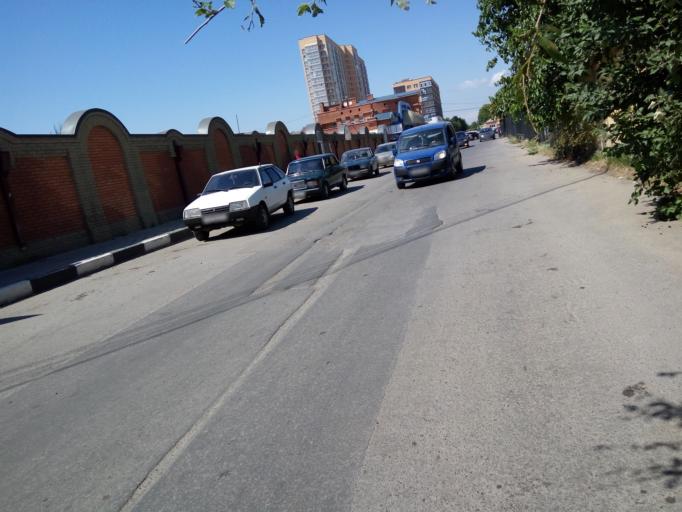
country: RU
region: Rostov
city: Bataysk
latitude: 47.1365
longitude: 39.7551
